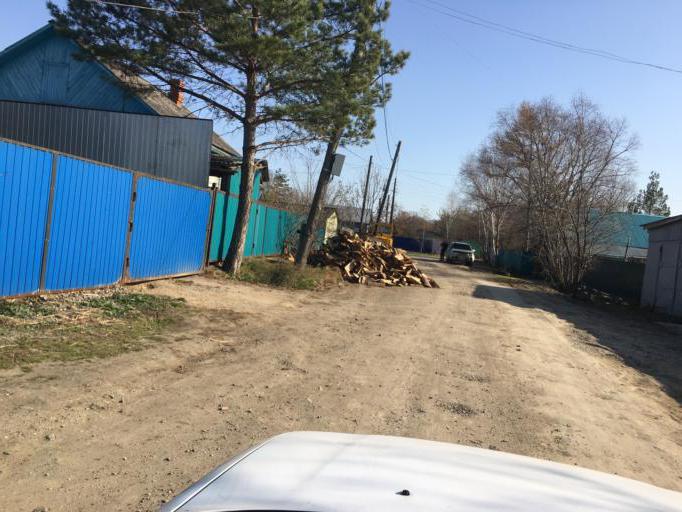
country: RU
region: Primorskiy
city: Dal'nerechensk
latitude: 45.9221
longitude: 133.7248
